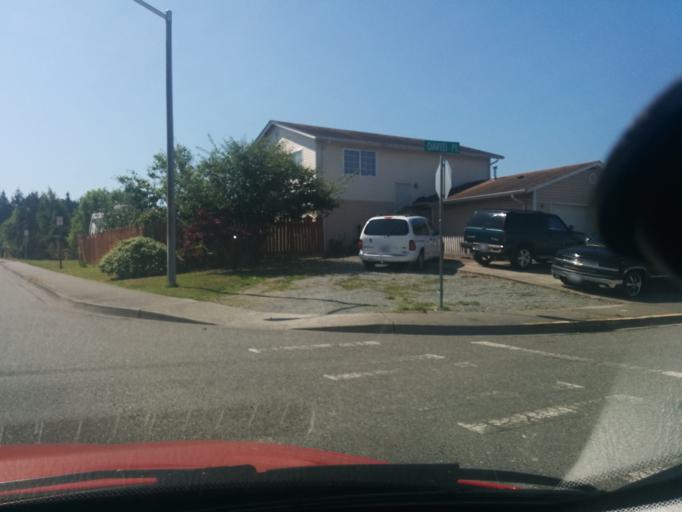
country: US
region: Washington
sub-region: Skagit County
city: Mount Vernon
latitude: 48.4310
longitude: -122.3027
